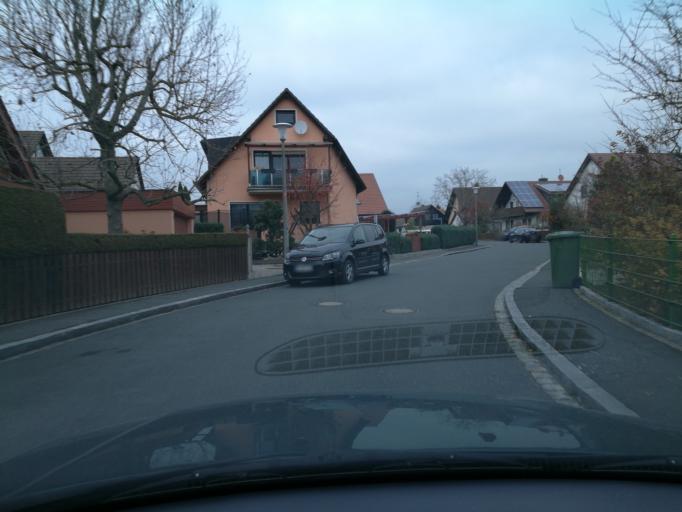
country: DE
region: Bavaria
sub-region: Regierungsbezirk Mittelfranken
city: Seukendorf
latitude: 49.4861
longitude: 10.8879
